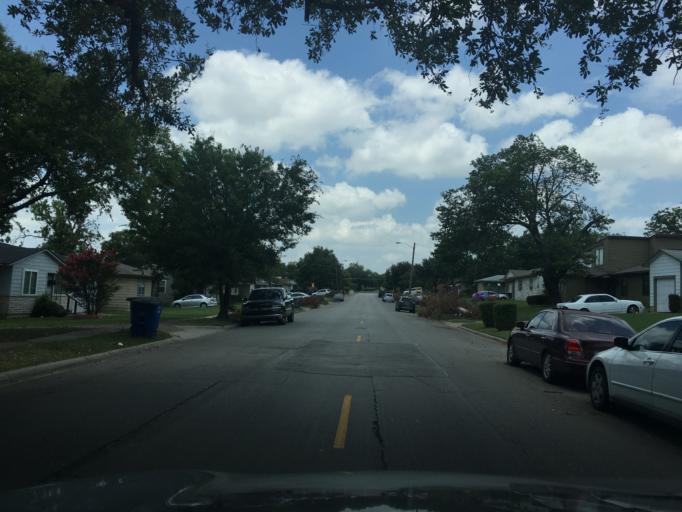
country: US
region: Texas
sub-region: Dallas County
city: Richardson
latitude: 32.9134
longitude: -96.7626
